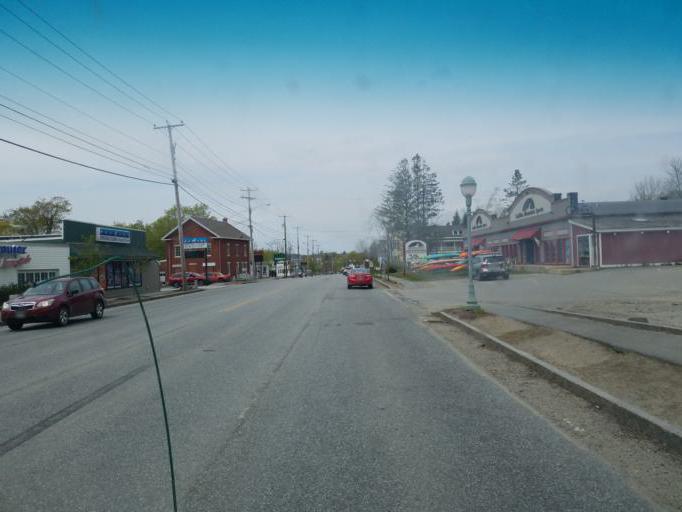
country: US
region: Maine
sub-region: Hancock County
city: Ellsworth
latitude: 44.5411
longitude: -68.4178
